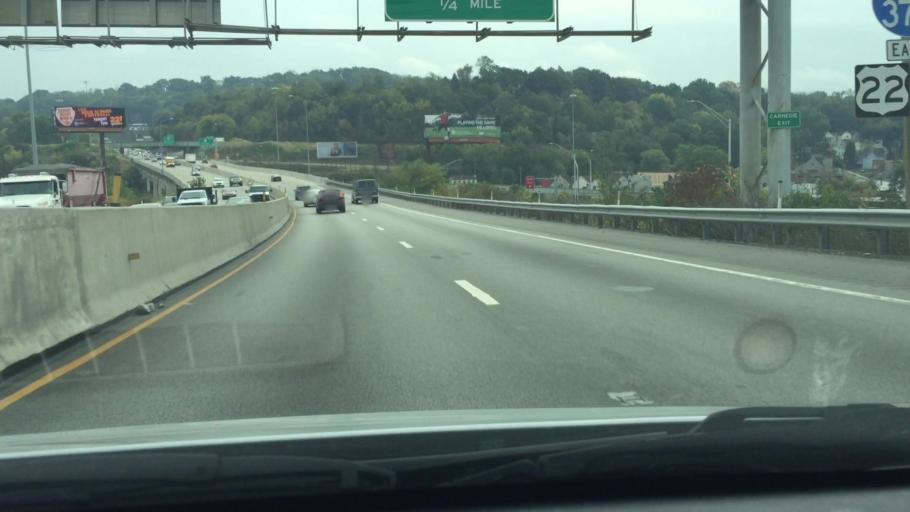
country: US
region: Pennsylvania
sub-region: Allegheny County
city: Carnegie
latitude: 40.4143
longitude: -80.0827
